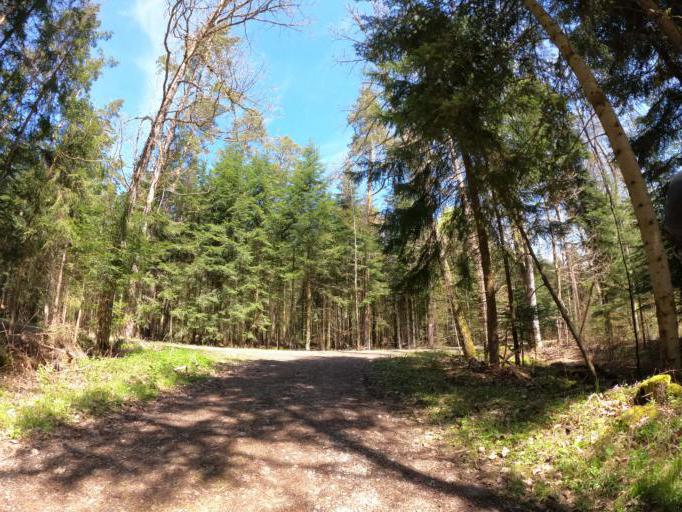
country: DE
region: Baden-Wuerttemberg
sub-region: Karlsruhe Region
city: Oberreichenbach
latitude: 48.7186
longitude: 8.6604
